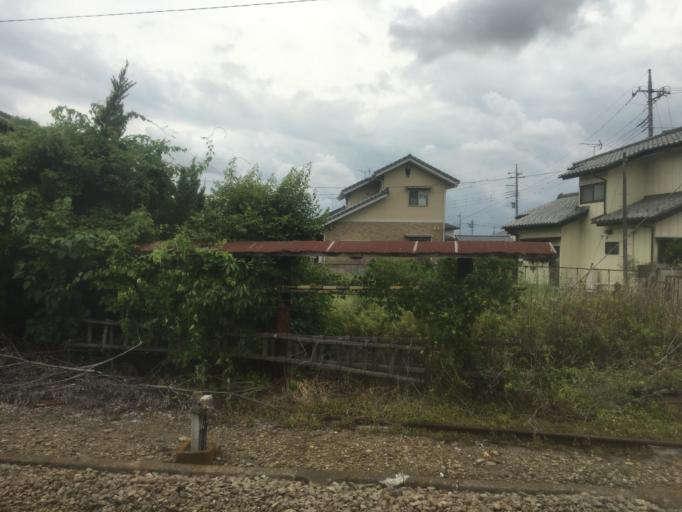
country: JP
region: Gunma
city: Fujioka
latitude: 36.2772
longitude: 139.0382
